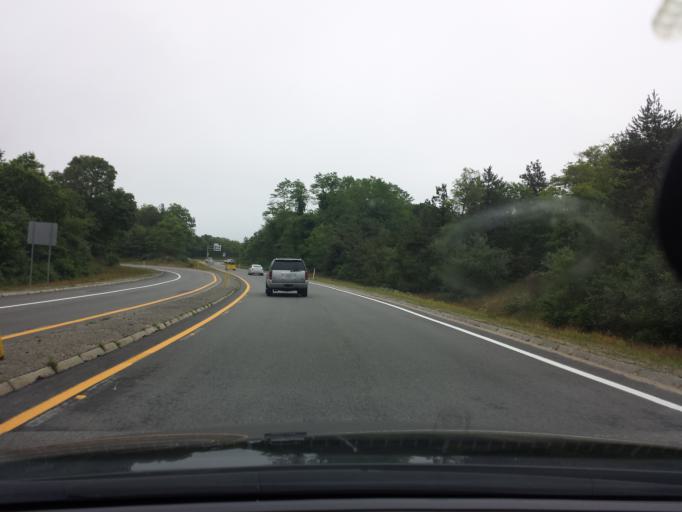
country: US
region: Massachusetts
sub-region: Barnstable County
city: Sagamore
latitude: 41.7691
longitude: -70.5461
